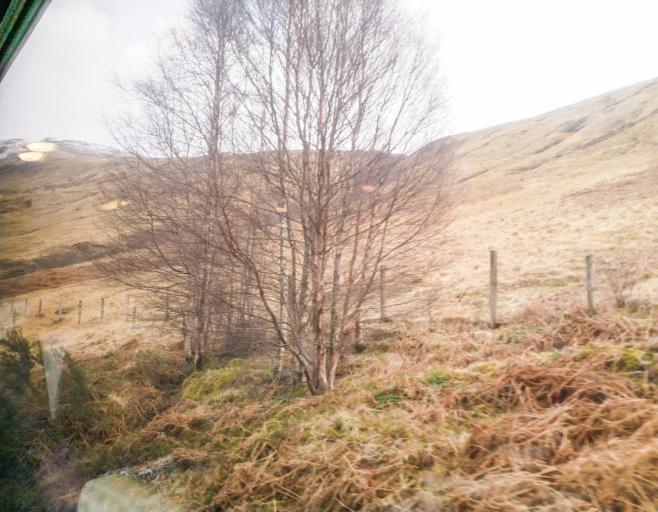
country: GB
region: Scotland
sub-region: Highland
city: Spean Bridge
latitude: 56.8125
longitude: -4.7162
